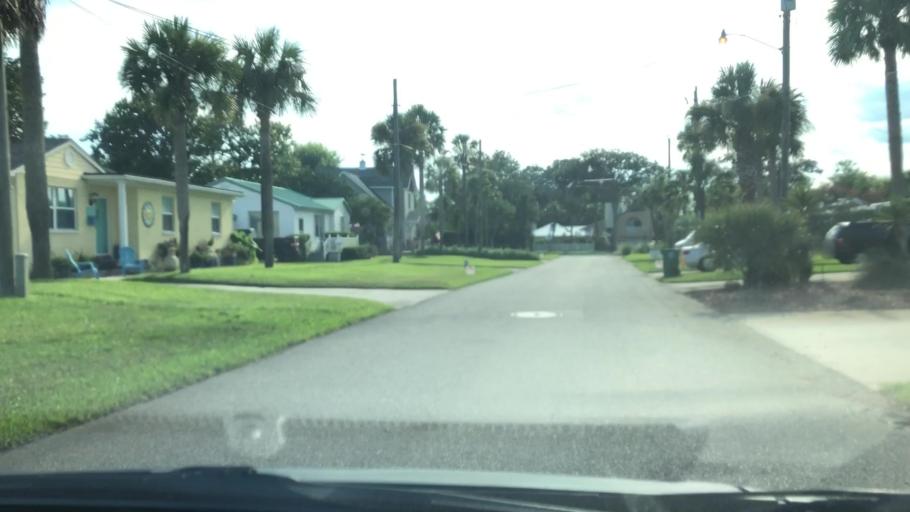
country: US
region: Florida
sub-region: Duval County
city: Jacksonville Beach
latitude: 30.3017
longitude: -81.3976
